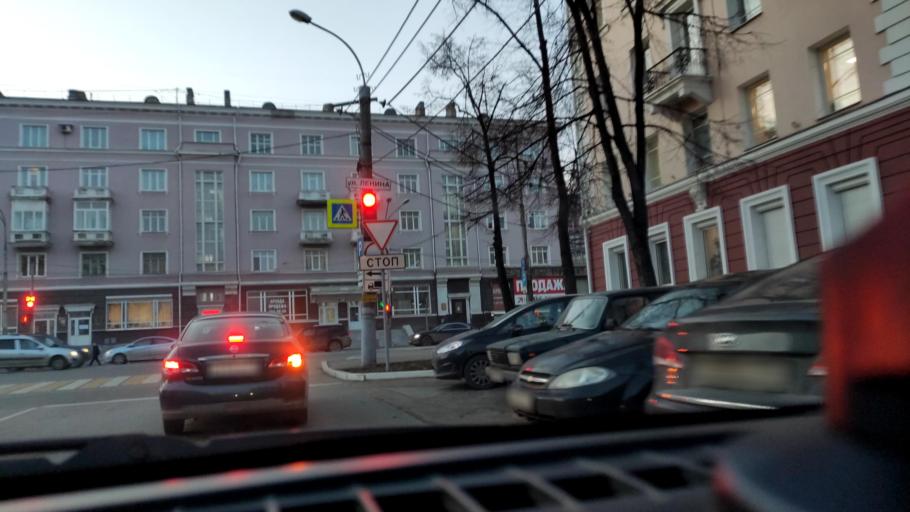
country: RU
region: Perm
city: Perm
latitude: 58.0053
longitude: 56.2022
